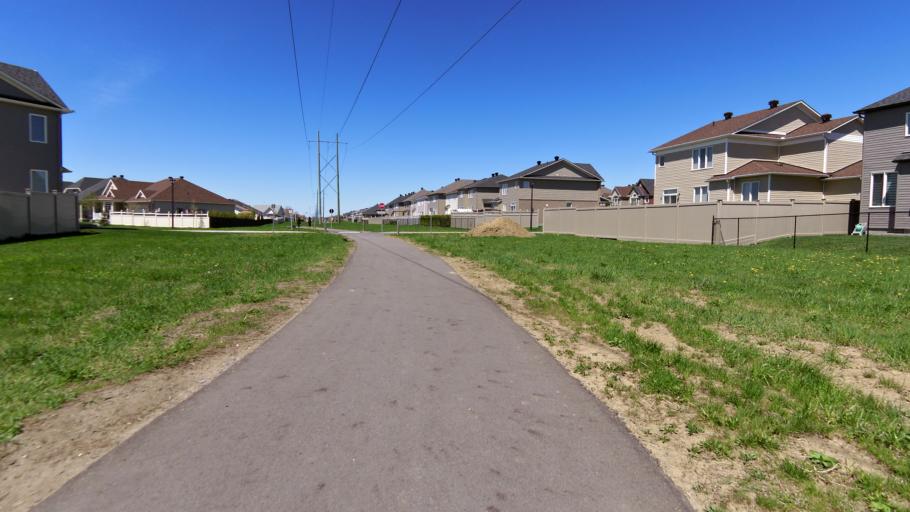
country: CA
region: Ontario
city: Clarence-Rockland
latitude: 45.4519
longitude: -75.4689
